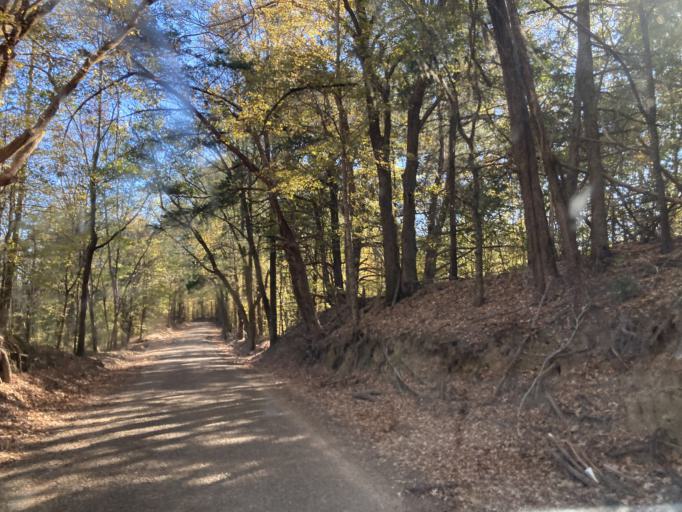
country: US
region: Mississippi
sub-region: Yazoo County
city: Yazoo City
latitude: 32.7826
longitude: -90.4080
